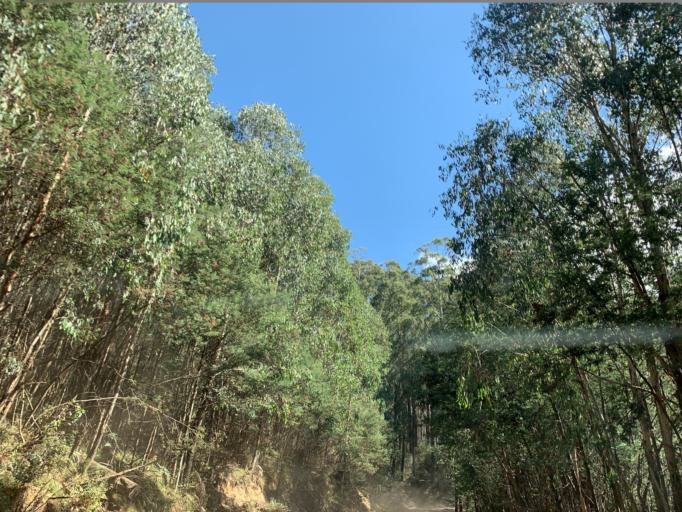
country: AU
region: Victoria
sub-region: Mansfield
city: Mansfield
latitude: -37.0975
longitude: 146.4725
